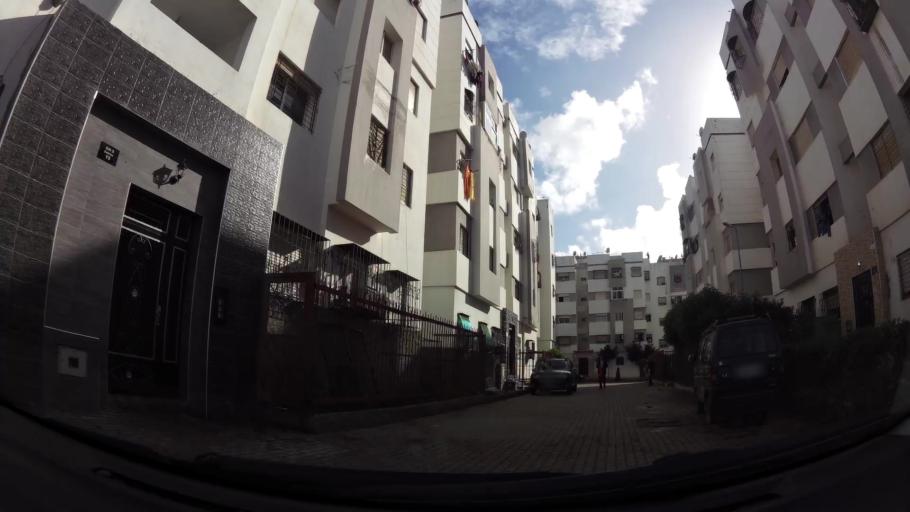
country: MA
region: Grand Casablanca
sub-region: Casablanca
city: Casablanca
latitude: 33.5565
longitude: -7.6993
